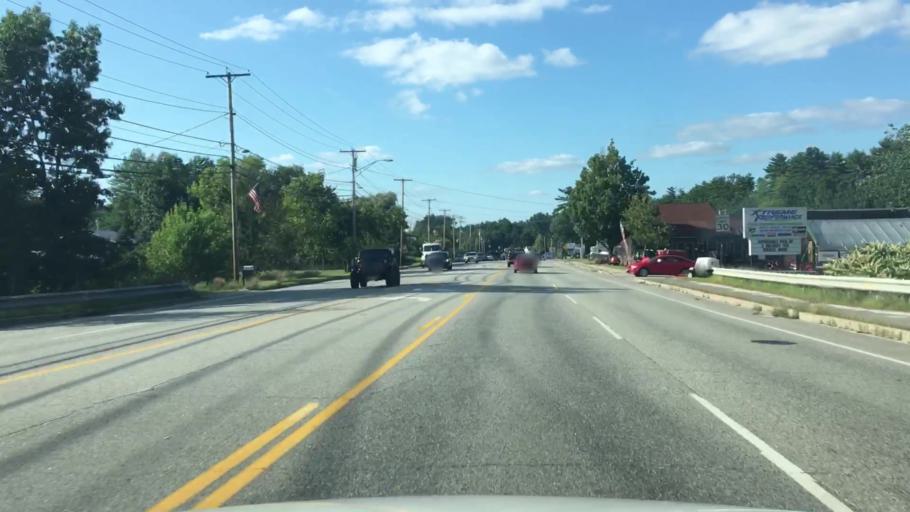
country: US
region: Maine
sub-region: Cumberland County
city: North Windham
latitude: 43.8451
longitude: -70.4470
